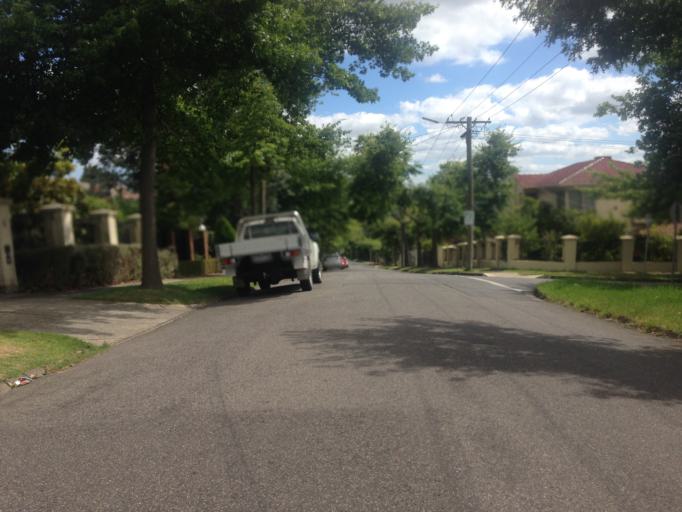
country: AU
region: Victoria
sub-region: Boroondara
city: Balwyn North
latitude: -37.7937
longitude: 145.0815
